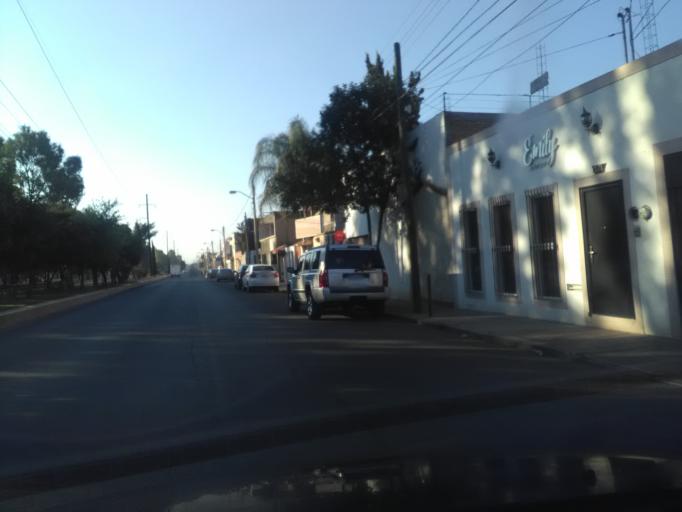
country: MX
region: Durango
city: Victoria de Durango
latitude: 24.0474
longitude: -104.6391
